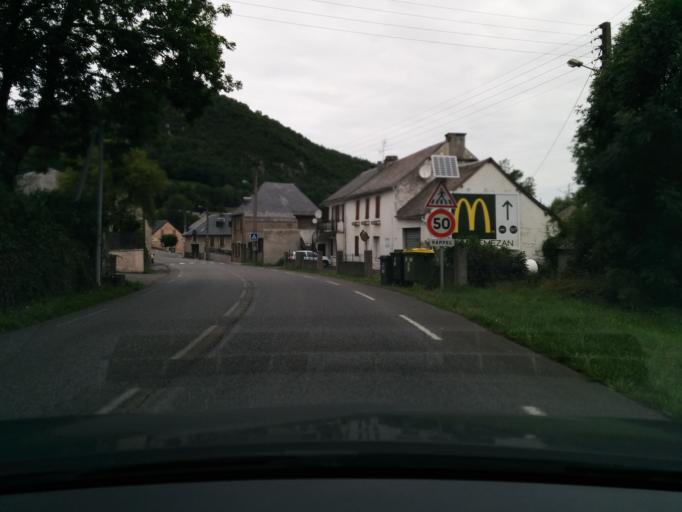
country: FR
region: Midi-Pyrenees
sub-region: Departement des Hautes-Pyrenees
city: La Barthe-de-Neste
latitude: 42.9935
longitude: 0.3748
